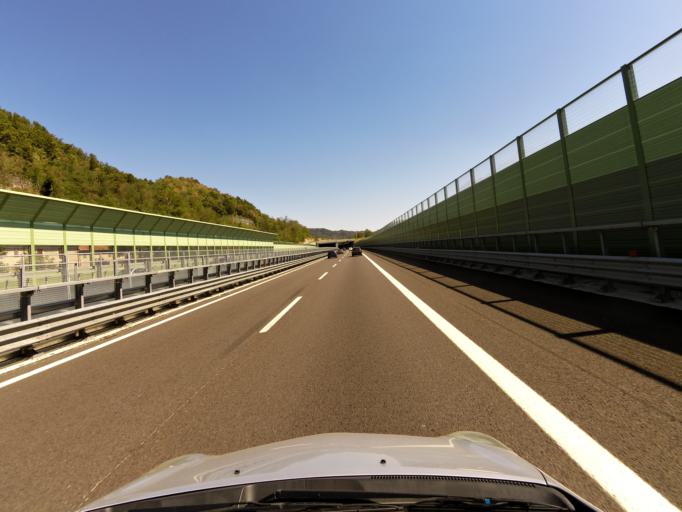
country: IT
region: Emilia-Romagna
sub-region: Provincia di Bologna
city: Grizzana
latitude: 44.2722
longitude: 11.1918
